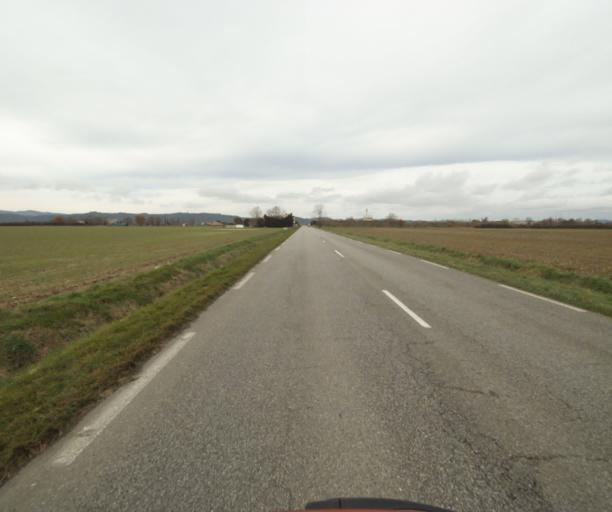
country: FR
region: Midi-Pyrenees
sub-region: Departement de l'Ariege
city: La Tour-du-Crieu
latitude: 43.0957
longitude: 1.6641
